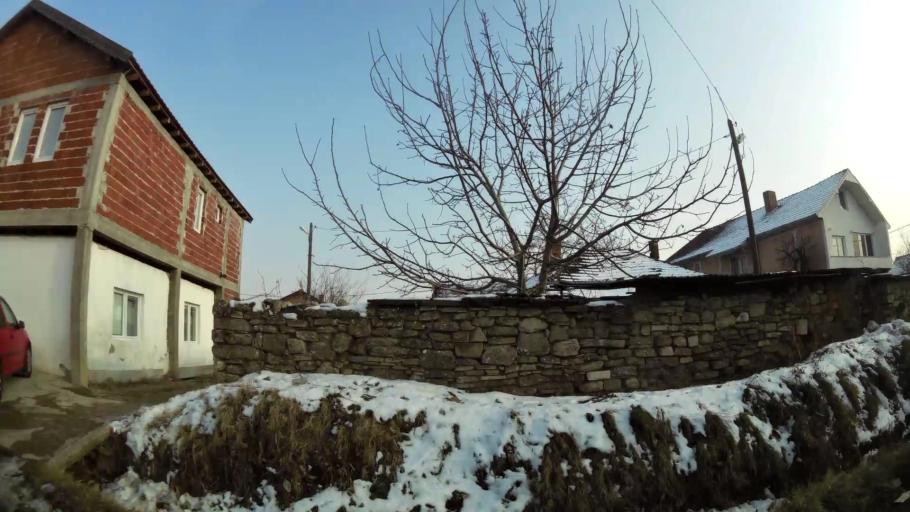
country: MK
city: Creshevo
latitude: 42.0227
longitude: 21.5101
